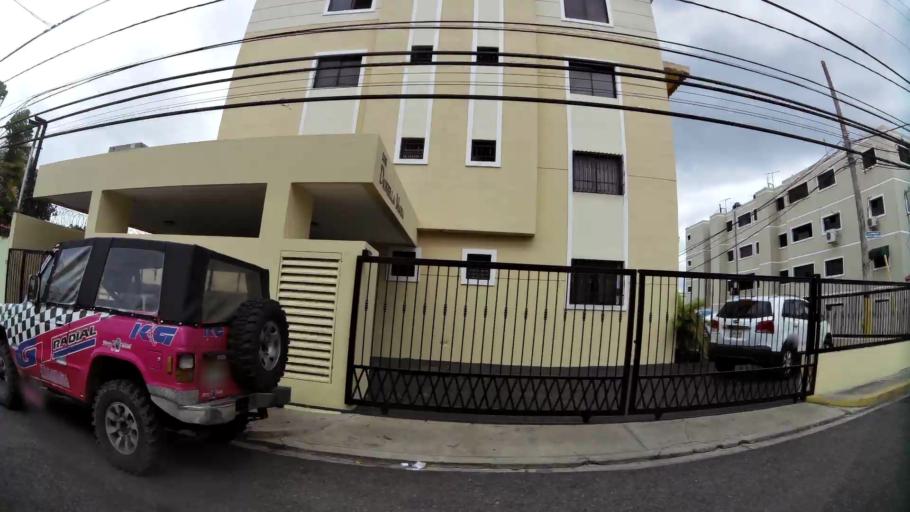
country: DO
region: Nacional
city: La Agustina
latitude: 18.4938
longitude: -69.9346
